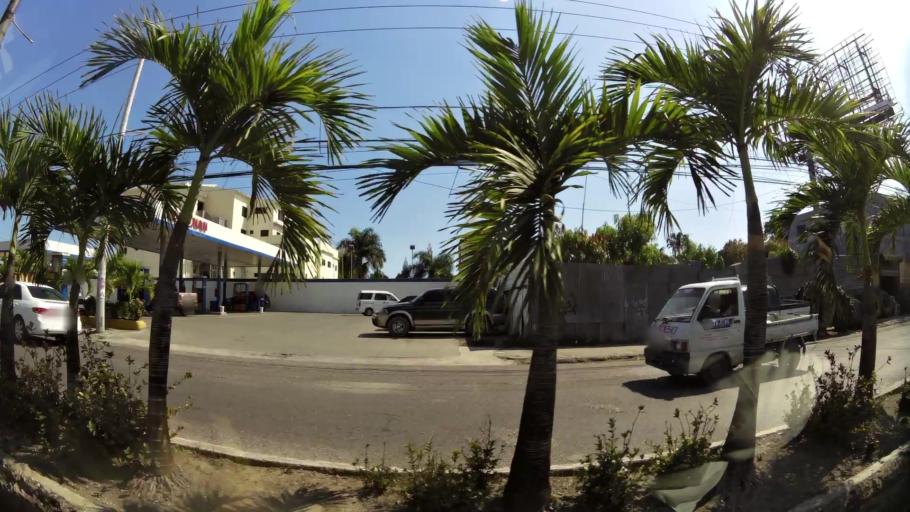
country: DO
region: Nacional
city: Santo Domingo
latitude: 18.4838
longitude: -69.9811
